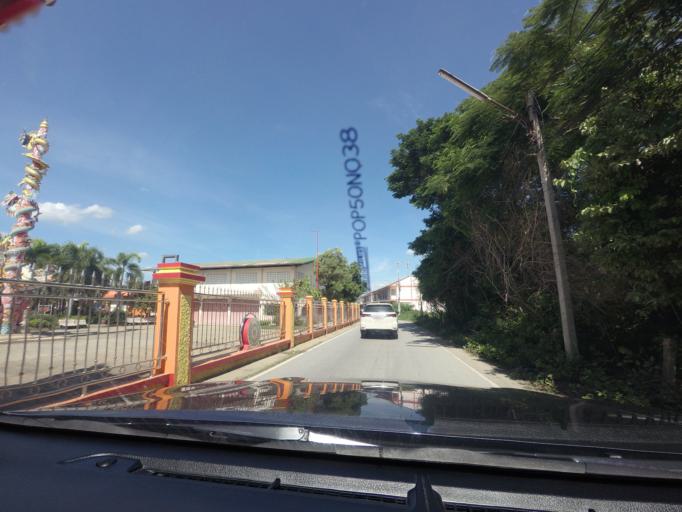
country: TH
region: Suphan Buri
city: Song Phi Nong
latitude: 14.1779
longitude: 99.9362
